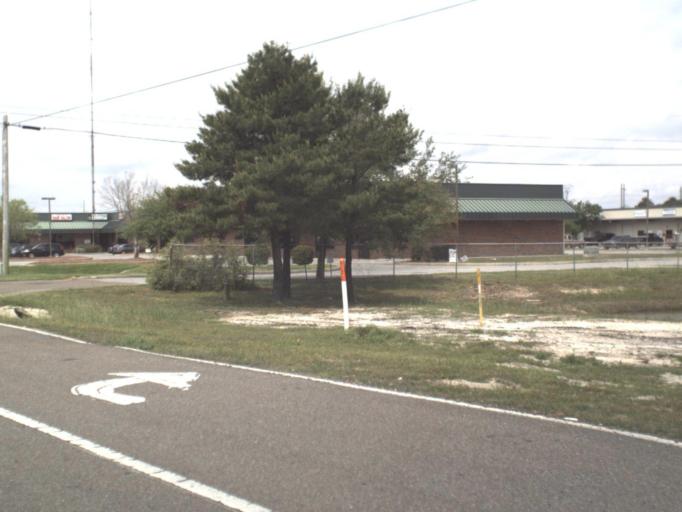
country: US
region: Florida
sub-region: Santa Rosa County
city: Woodlawn Beach
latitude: 30.4021
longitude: -86.9850
